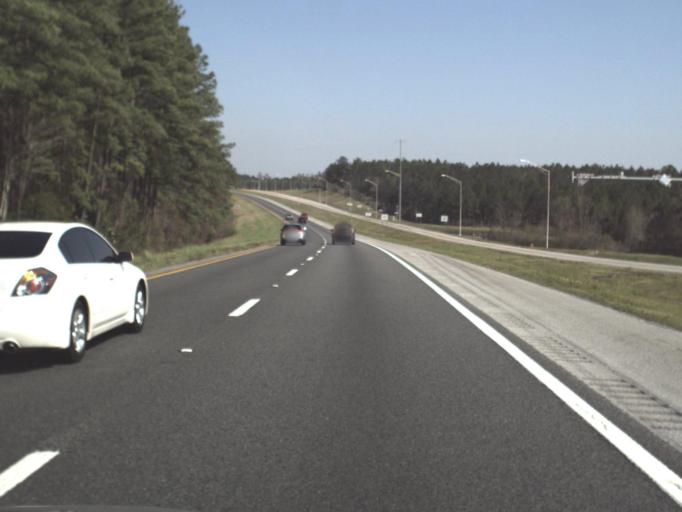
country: US
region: Florida
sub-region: Jackson County
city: Sneads
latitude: 30.6388
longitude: -84.9931
